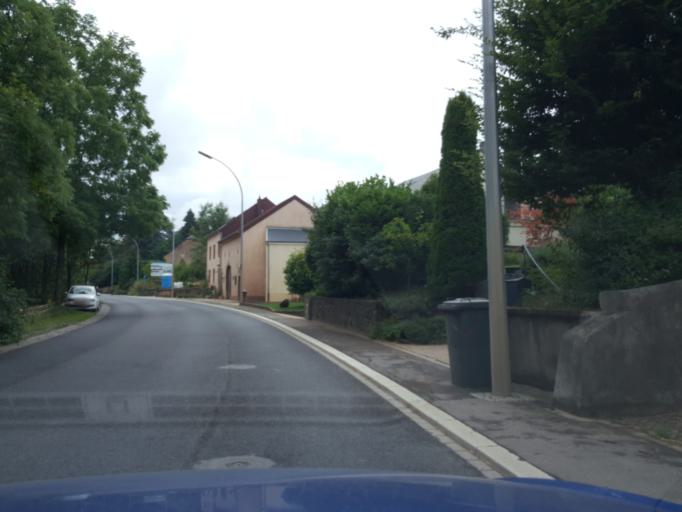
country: LU
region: Luxembourg
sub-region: Canton de Capellen
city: Kopstal
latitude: 49.6970
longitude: 6.0711
